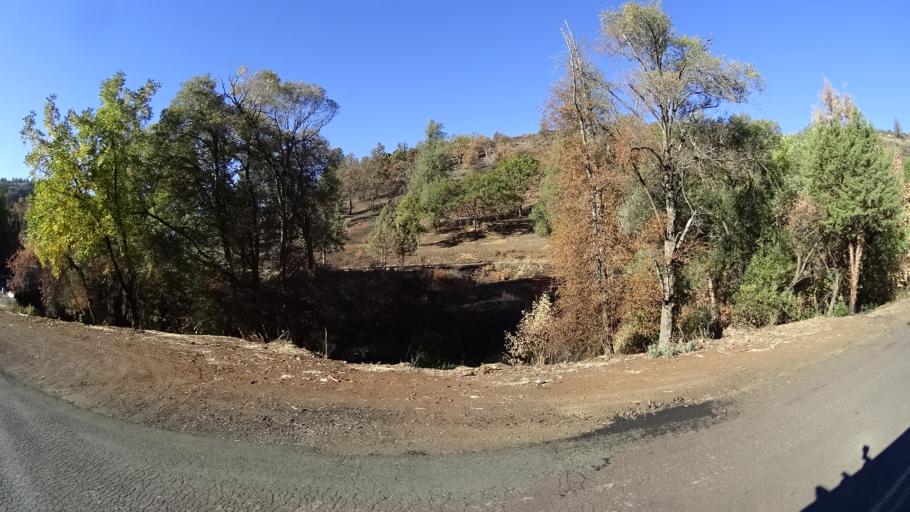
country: US
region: California
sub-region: Siskiyou County
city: Montague
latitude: 41.9330
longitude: -122.4413
